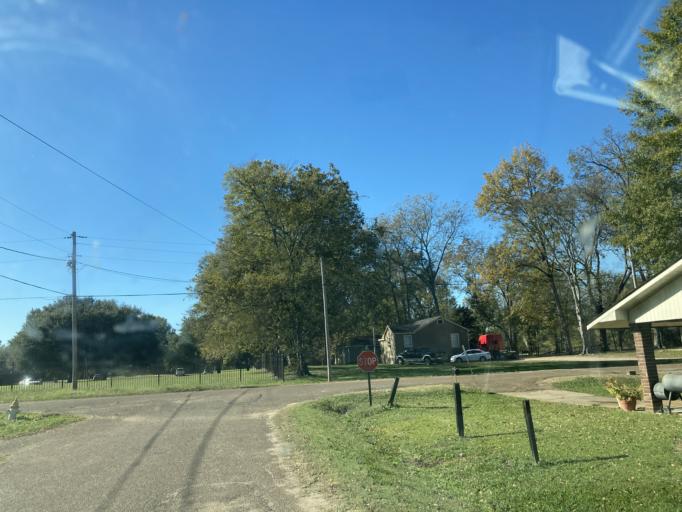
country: US
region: Mississippi
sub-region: Yazoo County
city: Yazoo City
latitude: 32.8434
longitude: -90.4248
